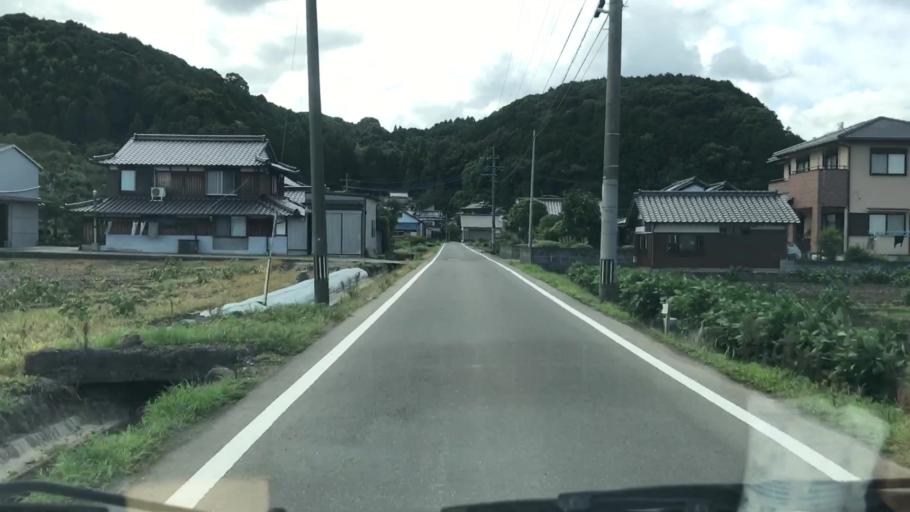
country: JP
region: Saga Prefecture
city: Kashima
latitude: 33.1173
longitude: 130.0719
